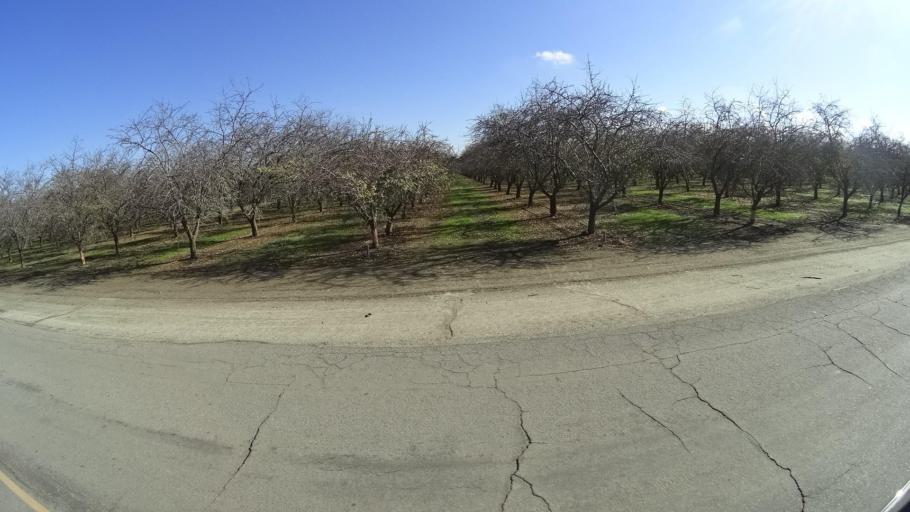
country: US
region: California
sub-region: Kern County
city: McFarland
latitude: 35.7053
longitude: -119.2586
